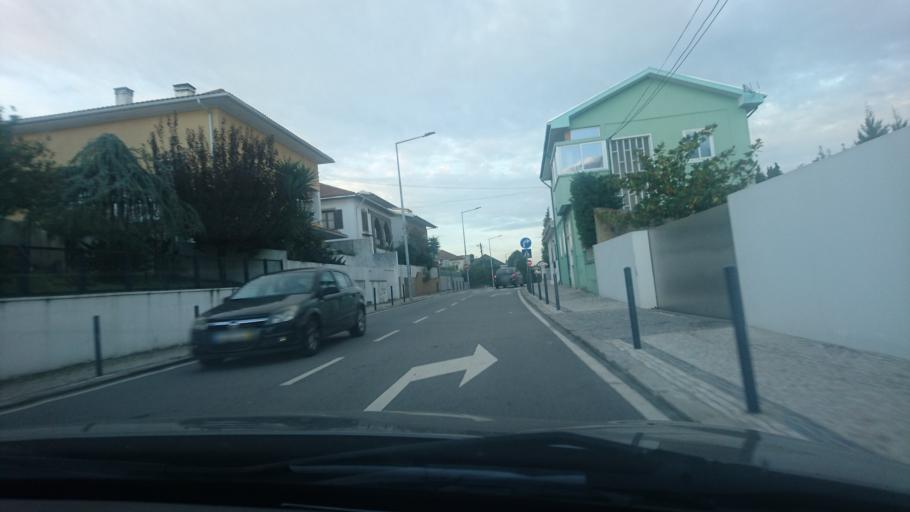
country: PT
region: Aveiro
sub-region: Sao Joao da Madeira
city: Sao Joao da Madeira
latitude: 40.8931
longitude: -8.4904
